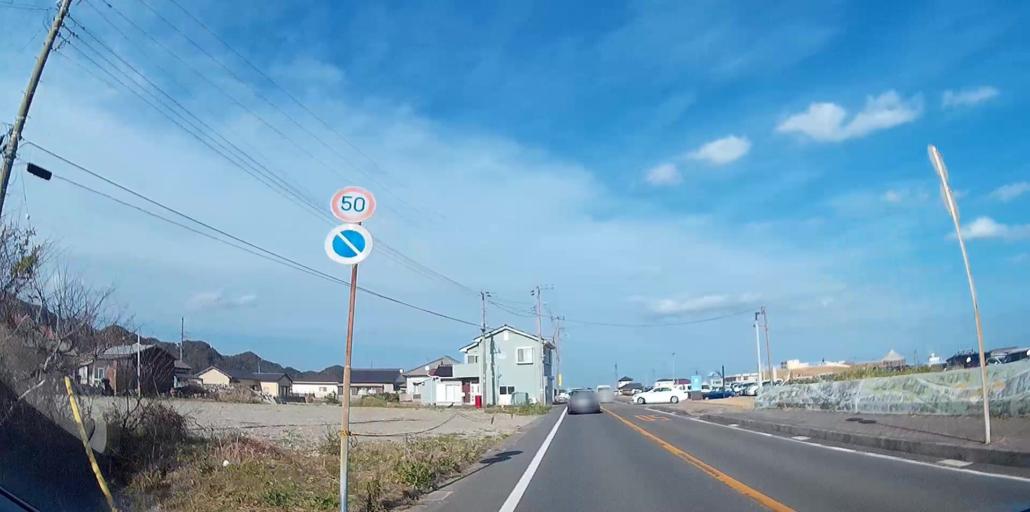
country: JP
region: Chiba
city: Tateyama
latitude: 34.9288
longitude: 139.9495
